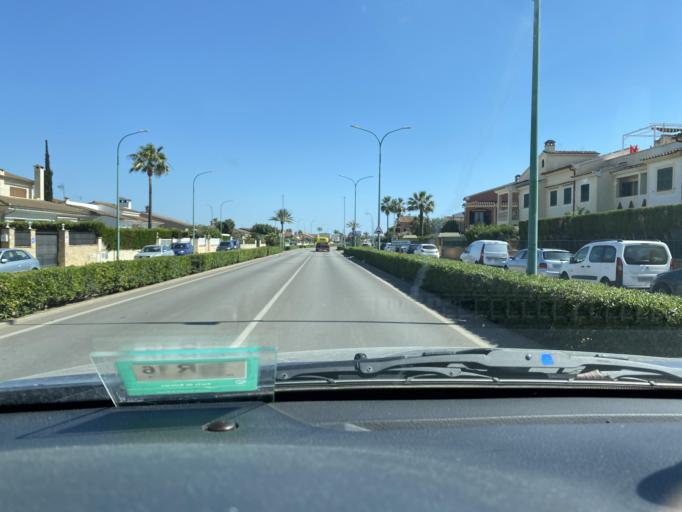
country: ES
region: Balearic Islands
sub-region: Illes Balears
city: Palma
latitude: 39.6130
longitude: 2.6840
